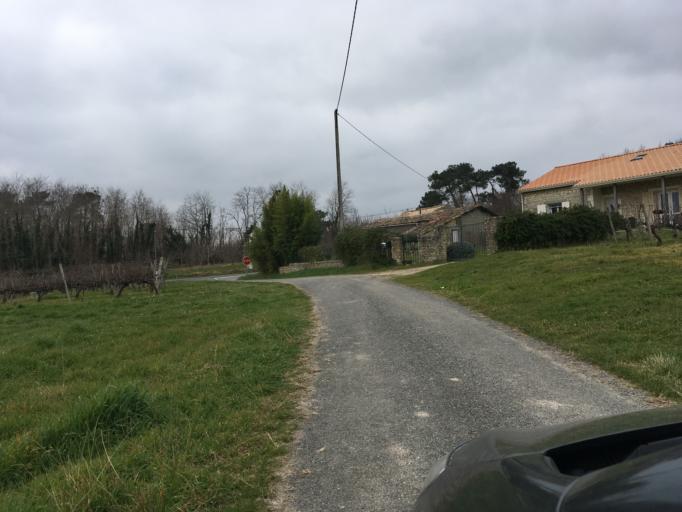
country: FR
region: Aquitaine
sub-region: Departement de la Gironde
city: Saint-Ciers-sur-Gironde
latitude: 45.3246
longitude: -0.5933
